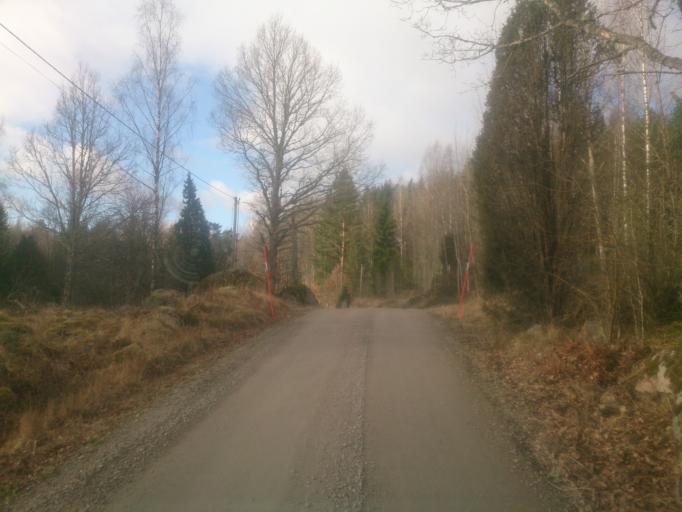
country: SE
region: OEstergoetland
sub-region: Atvidabergs Kommun
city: Atvidaberg
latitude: 58.2246
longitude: 16.1742
